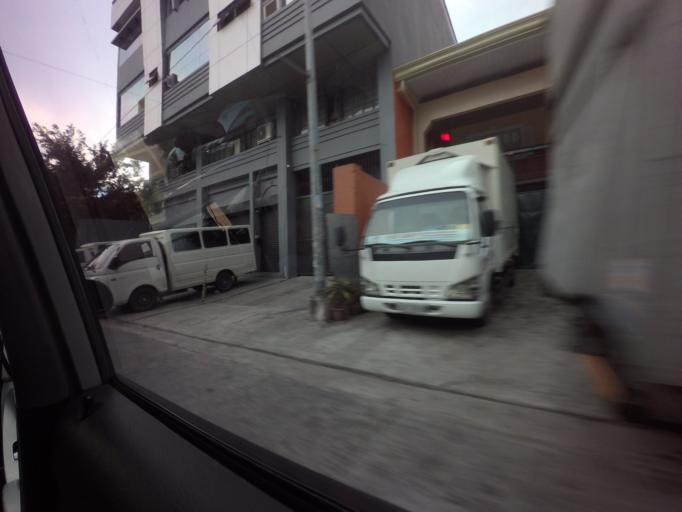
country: PH
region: Metro Manila
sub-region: City of Manila
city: Manila
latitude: 14.6165
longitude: 121.0050
